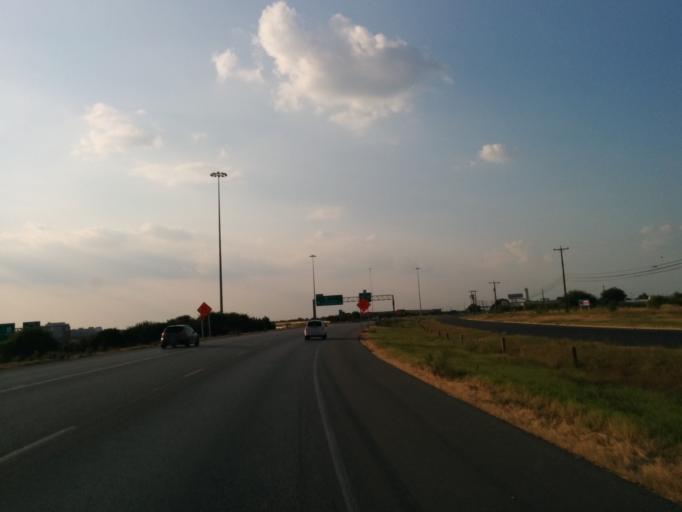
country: US
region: Texas
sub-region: Bexar County
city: Kirby
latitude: 29.4486
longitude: -98.4029
